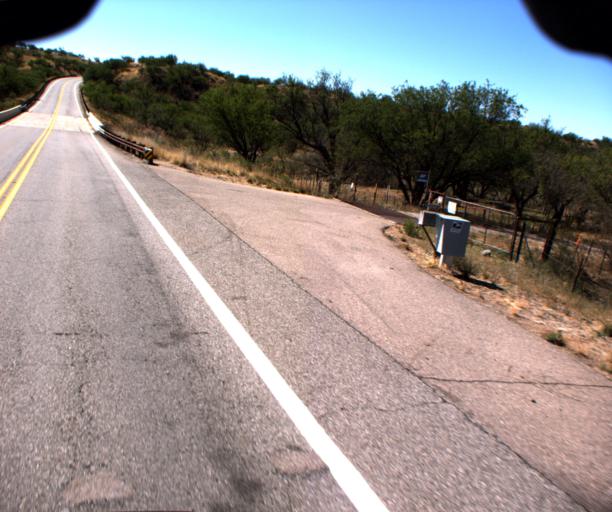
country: US
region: Arizona
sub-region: Santa Cruz County
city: Nogales
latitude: 31.4338
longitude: -110.8441
